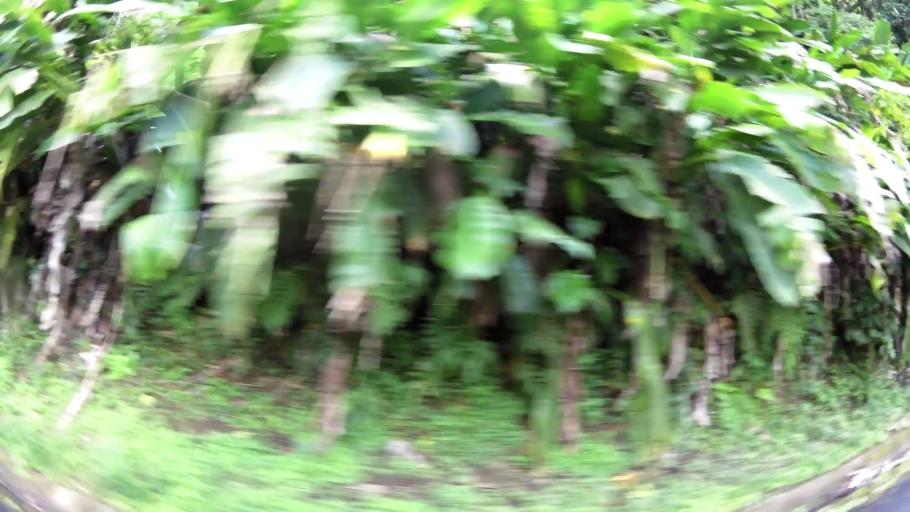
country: MQ
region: Martinique
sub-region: Martinique
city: Saint-Joseph
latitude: 14.6781
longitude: -61.0856
